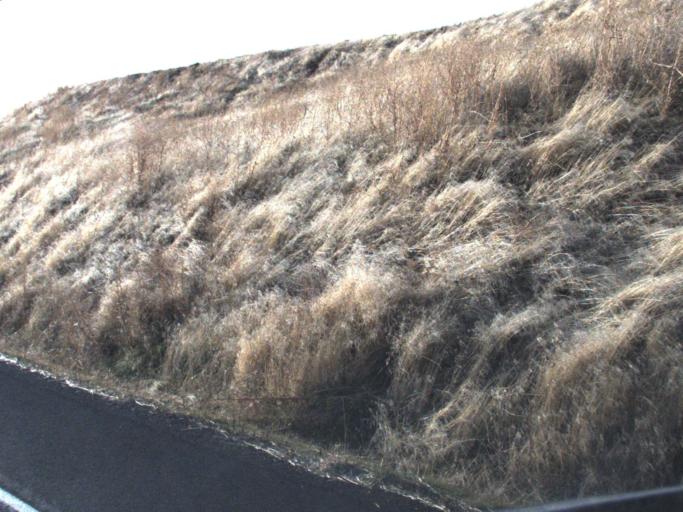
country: US
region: Washington
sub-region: Columbia County
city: Dayton
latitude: 46.3542
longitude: -117.9566
